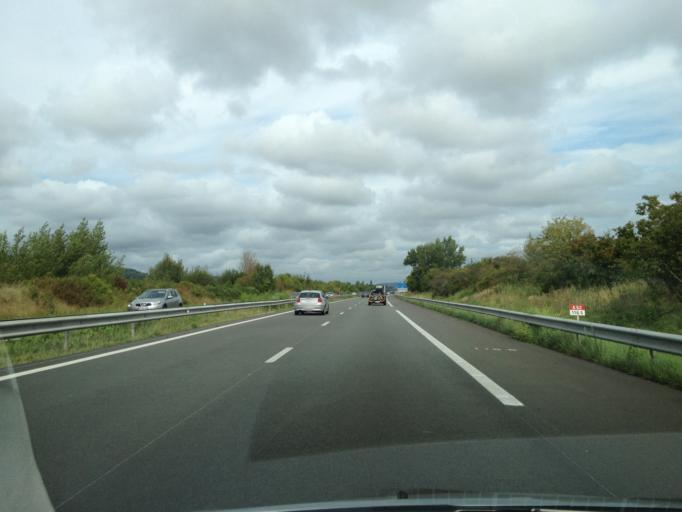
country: FR
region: Aquitaine
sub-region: Departement du Lot-et-Garonne
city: Sainte-Colombe-en-Bruilhois
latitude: 44.1914
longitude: 0.5211
